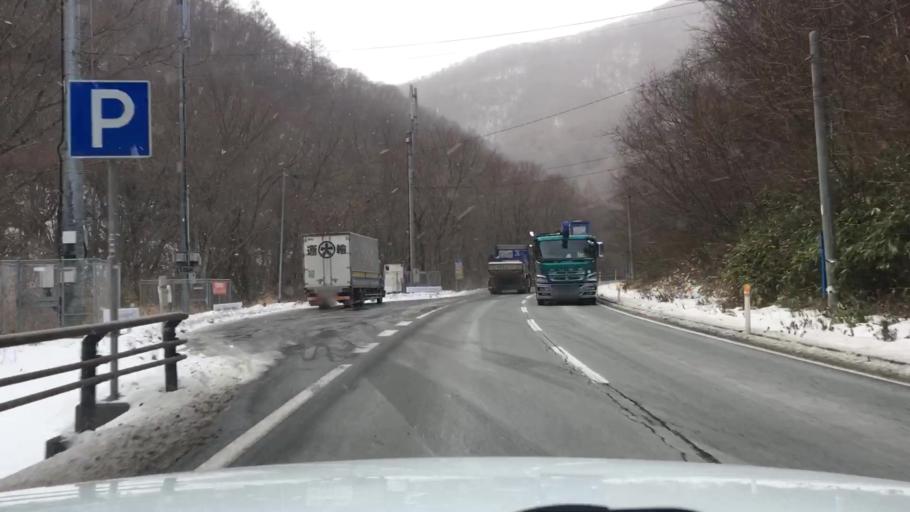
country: JP
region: Iwate
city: Tono
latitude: 39.6167
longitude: 141.4993
